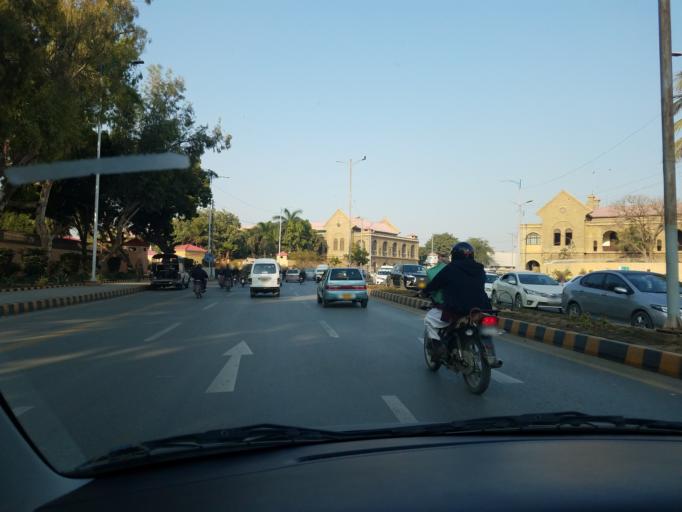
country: PK
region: Sindh
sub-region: Karachi District
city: Karachi
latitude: 24.8542
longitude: 67.0356
